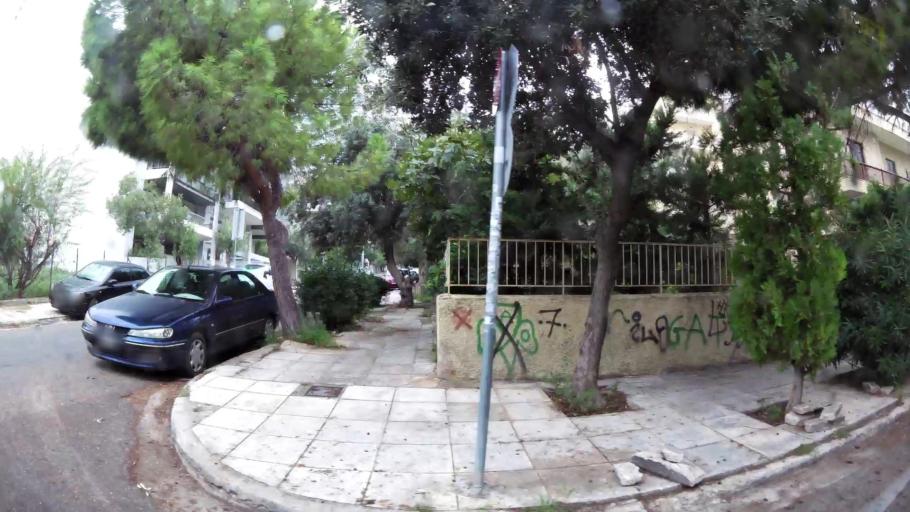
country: GR
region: Attica
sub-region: Nomarchia Athinas
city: Palaio Faliro
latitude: 37.9300
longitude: 23.7004
